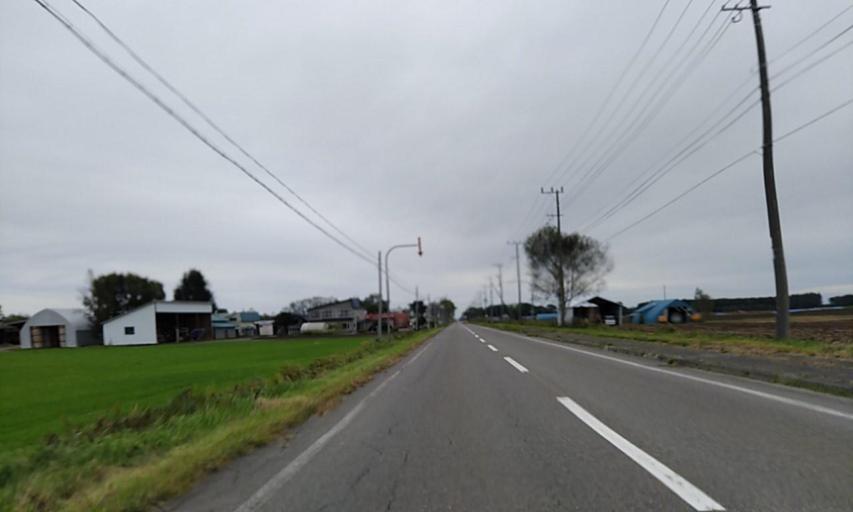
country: JP
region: Hokkaido
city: Obihiro
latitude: 42.6414
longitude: 143.0952
